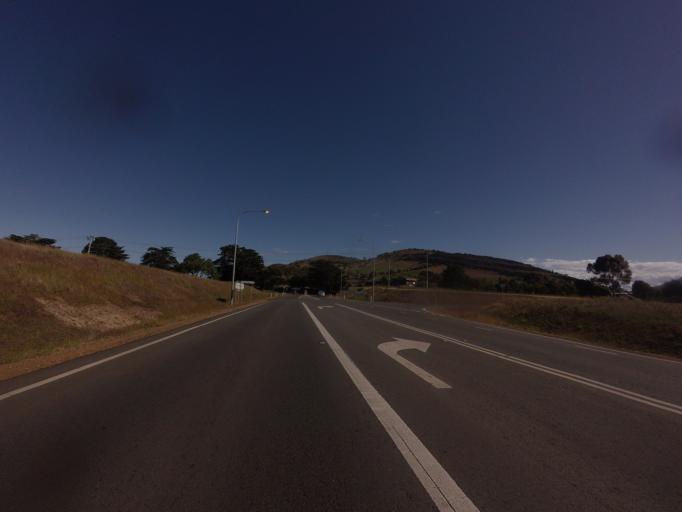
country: AU
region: Tasmania
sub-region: Clarence
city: Cambridge
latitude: -42.7373
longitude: 147.4302
